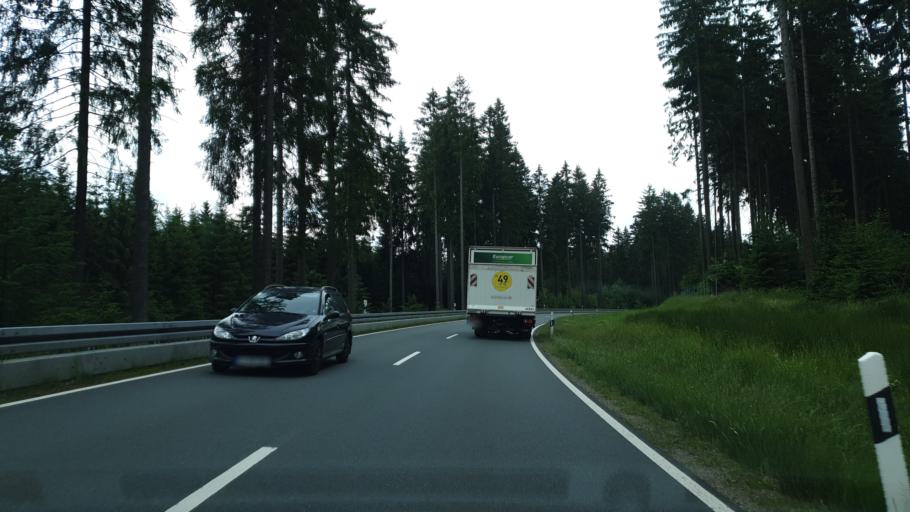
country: DE
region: Saxony
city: Tannenbergsthal
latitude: 50.4592
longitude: 12.4502
